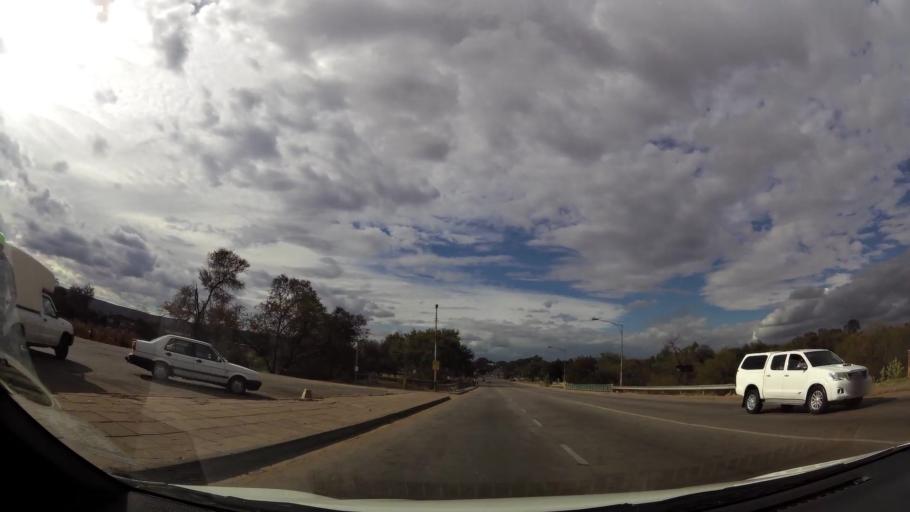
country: ZA
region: Limpopo
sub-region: Waterberg District Municipality
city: Modimolle
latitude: -24.6996
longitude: 28.4063
